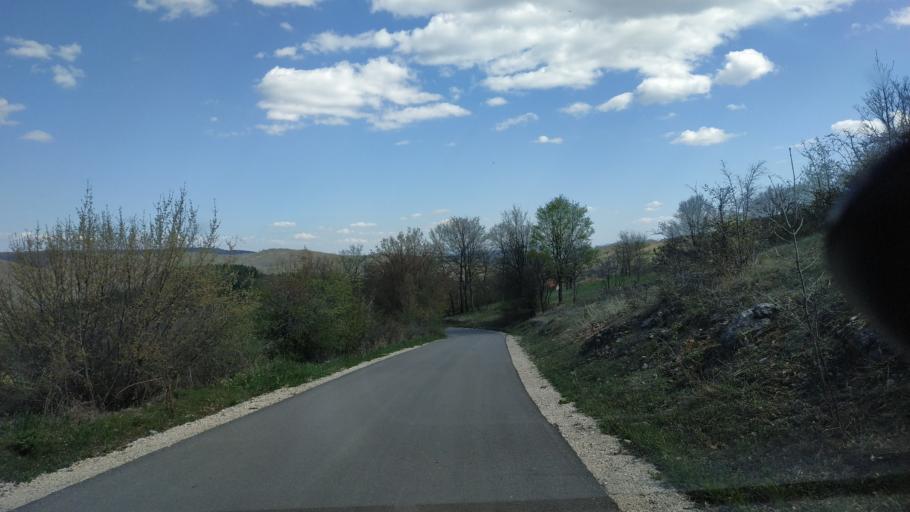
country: RS
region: Central Serbia
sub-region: Zajecarski Okrug
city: Soko Banja
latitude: 43.5758
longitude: 21.8949
